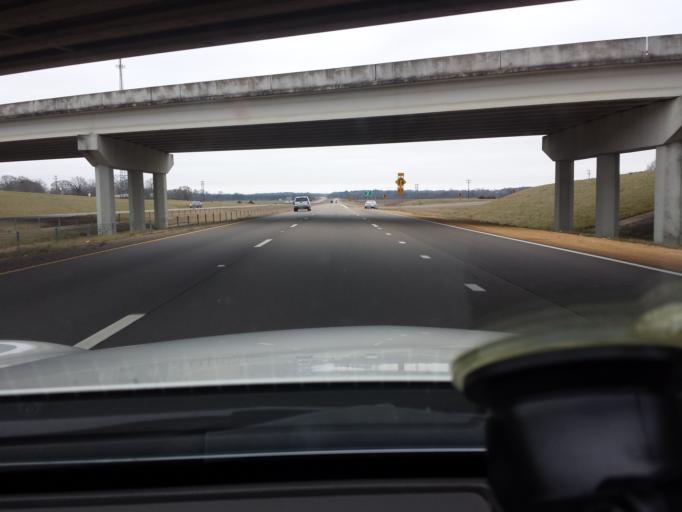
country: US
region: Mississippi
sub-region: Lee County
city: Shannon
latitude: 34.1170
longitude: -88.7015
